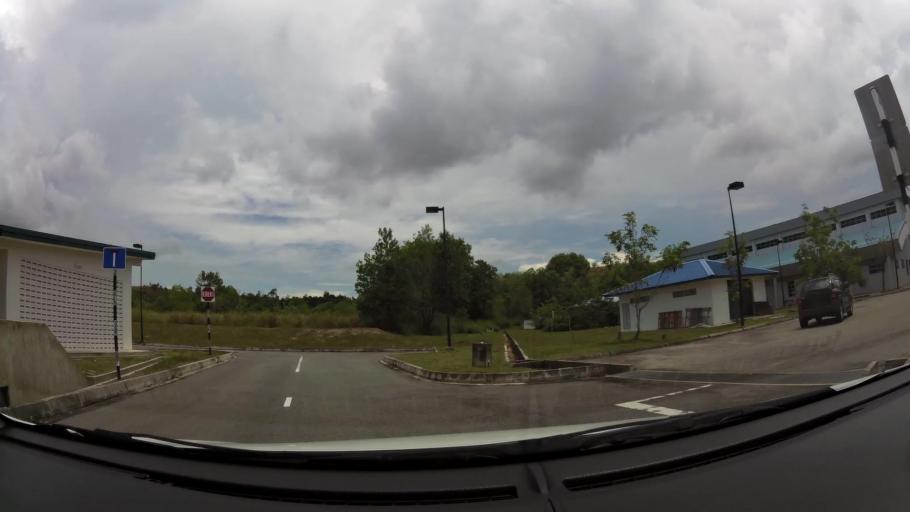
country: BN
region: Brunei and Muara
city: Bandar Seri Begawan
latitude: 4.9785
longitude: 114.9021
